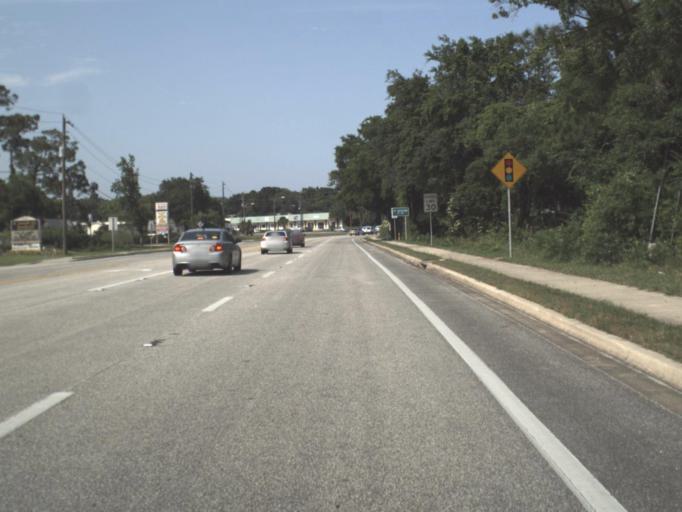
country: US
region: Florida
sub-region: Saint Johns County
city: Saint Augustine
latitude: 29.8787
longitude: -81.3282
